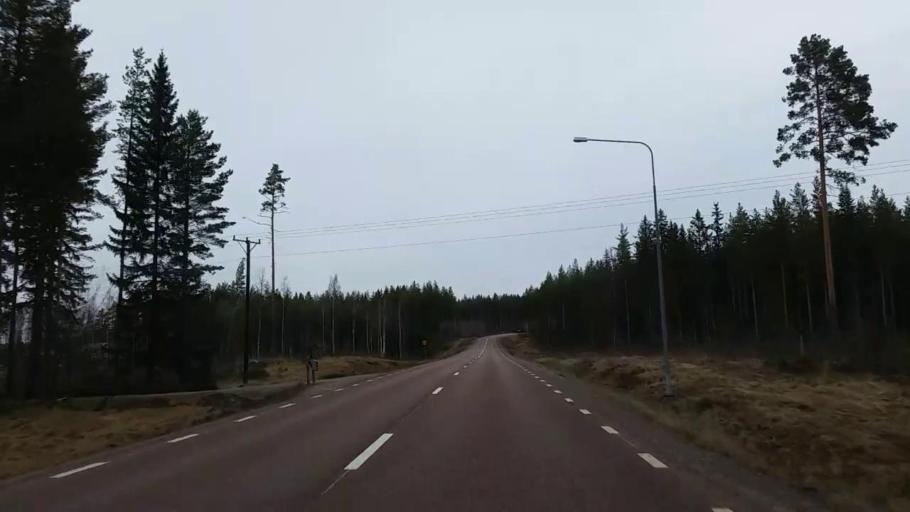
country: SE
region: Gaevleborg
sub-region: Ovanakers Kommun
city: Edsbyn
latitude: 61.2079
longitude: 15.8711
